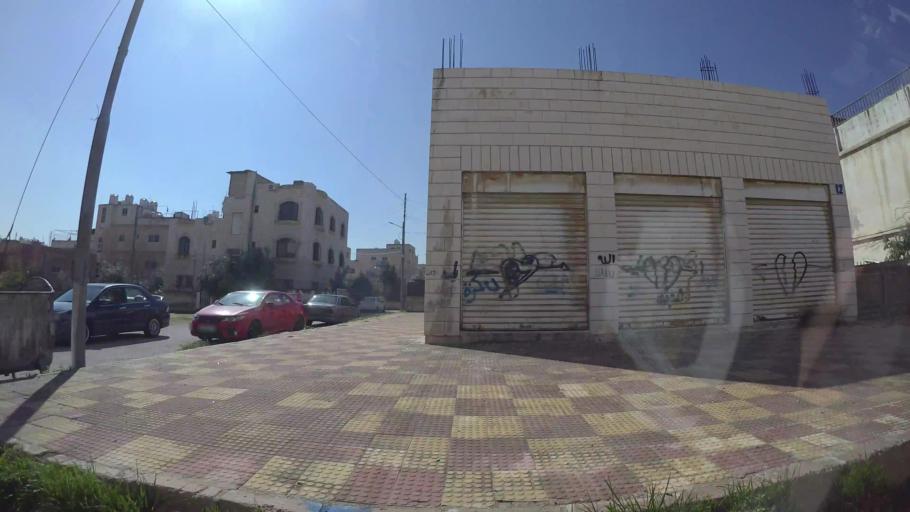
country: JO
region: Amman
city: Amman
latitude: 31.9887
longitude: 35.9812
